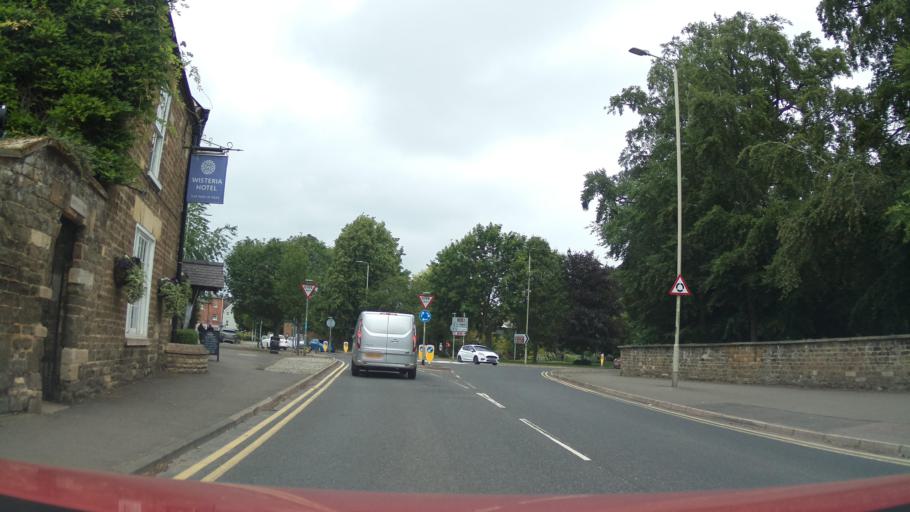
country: GB
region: England
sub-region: District of Rutland
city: Oakham
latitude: 52.6684
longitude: -0.7253
